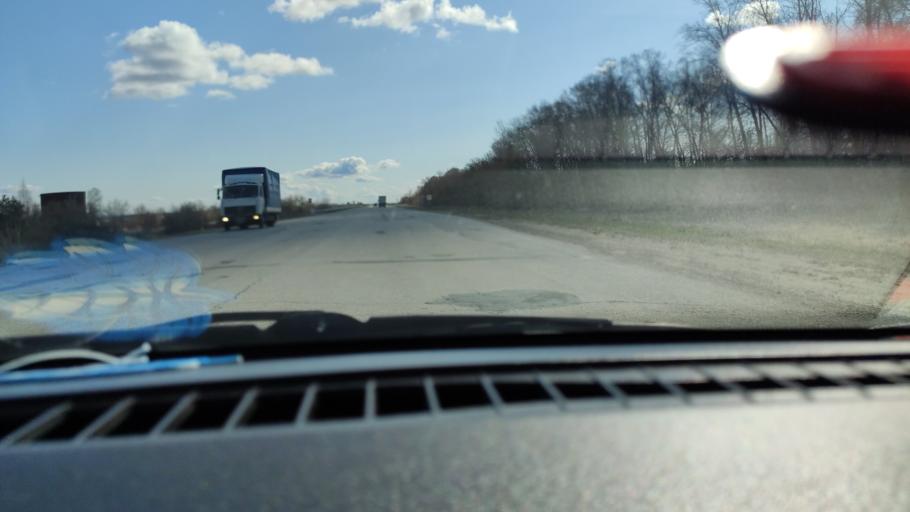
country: RU
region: Samara
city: Varlamovo
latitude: 53.1220
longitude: 48.3139
